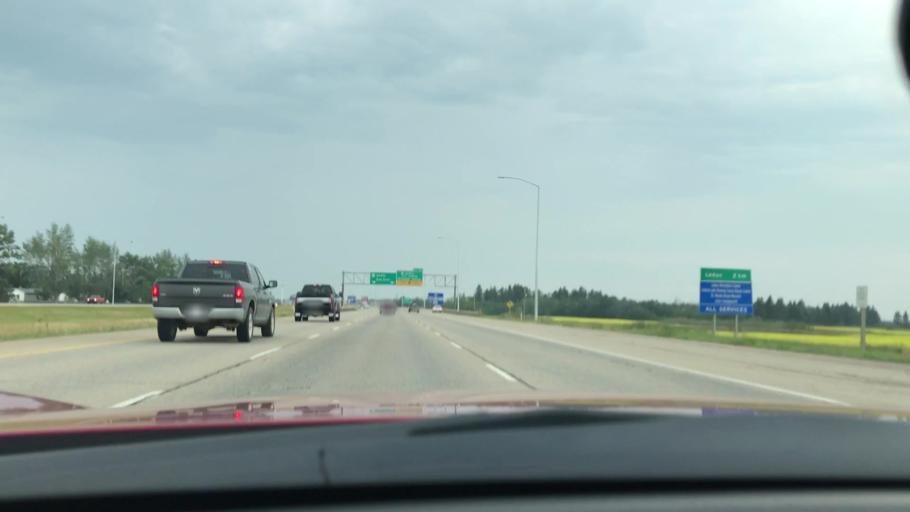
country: CA
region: Alberta
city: Leduc
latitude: 53.2756
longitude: -113.5558
